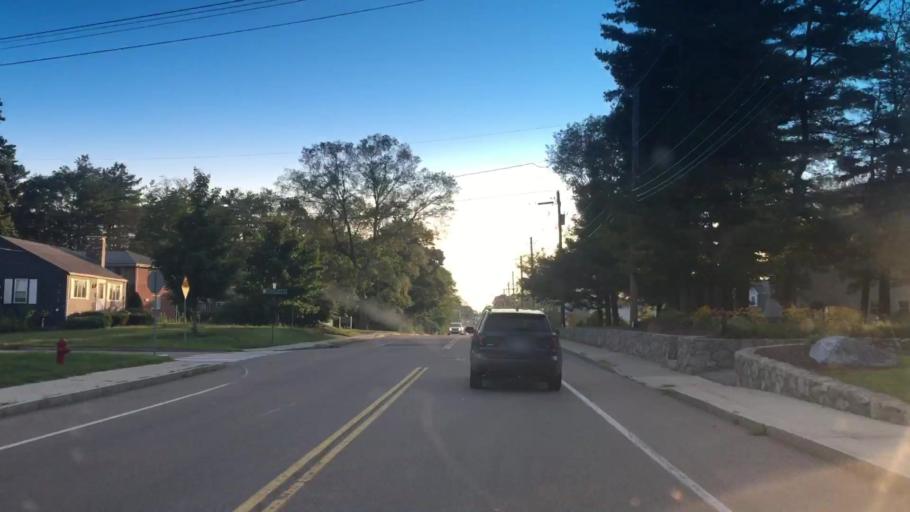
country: US
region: Massachusetts
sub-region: Norfolk County
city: Millis-Clicquot
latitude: 42.1754
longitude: -71.3392
